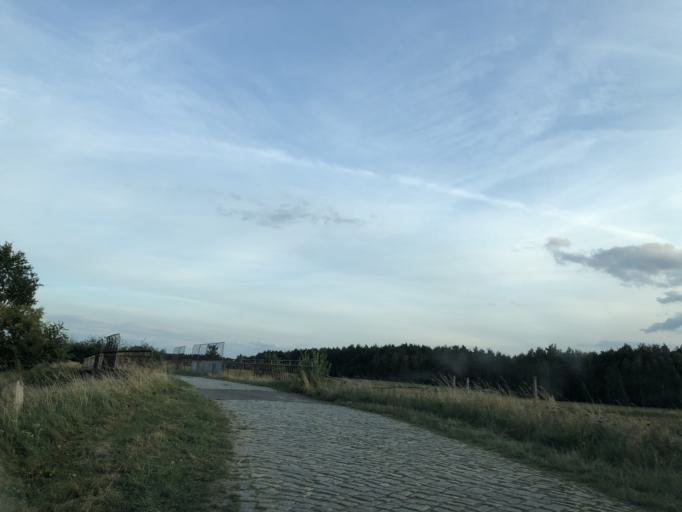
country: PL
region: Lubusz
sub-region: Powiat swiebodzinski
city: Zbaszynek
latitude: 52.2302
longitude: 15.8013
